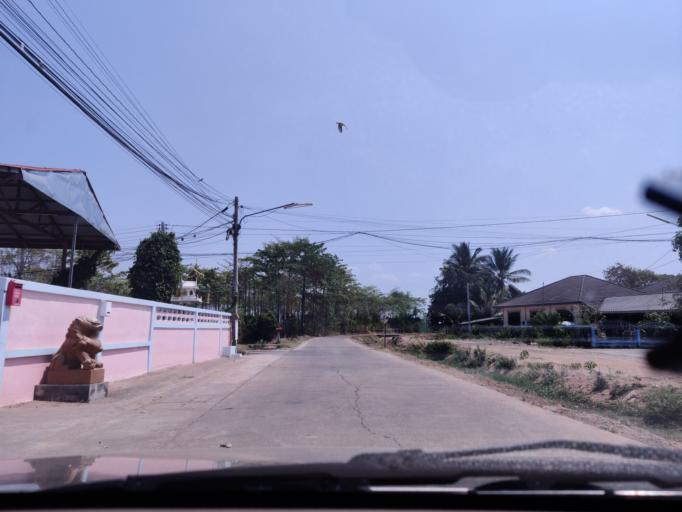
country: TH
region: Sisaket
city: Si Sa Ket
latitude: 15.1078
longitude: 104.3543
